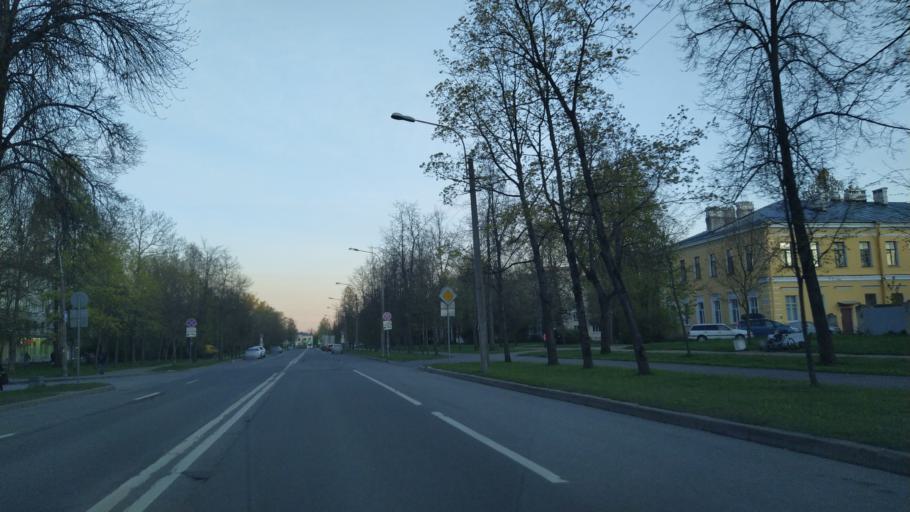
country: RU
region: St.-Petersburg
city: Pushkin
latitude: 59.7063
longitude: 30.4051
